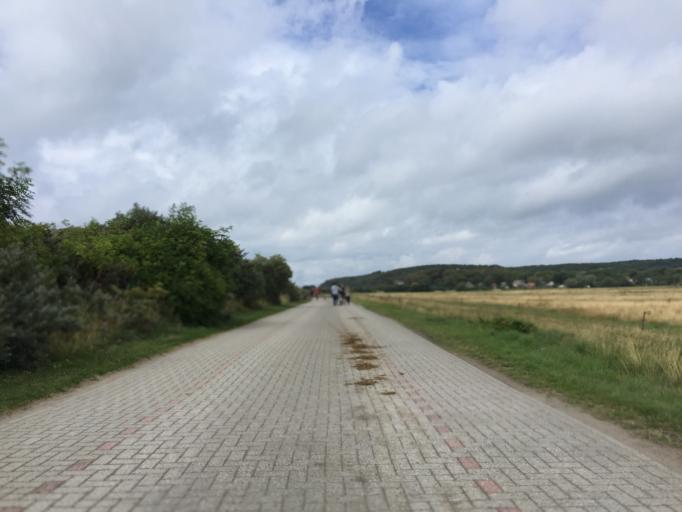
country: DE
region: Mecklenburg-Vorpommern
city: Hiddensee
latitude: 54.5773
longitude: 13.1040
